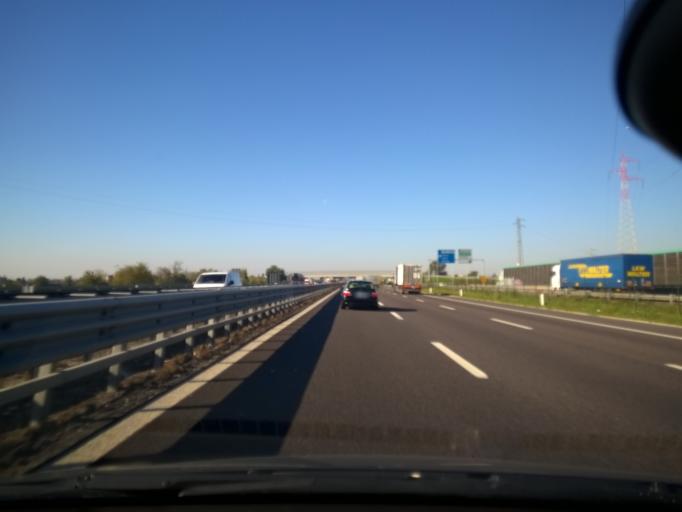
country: IT
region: Veneto
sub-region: Provincia di Verona
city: Beccacivetta-Azzano
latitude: 45.3996
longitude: 10.9500
